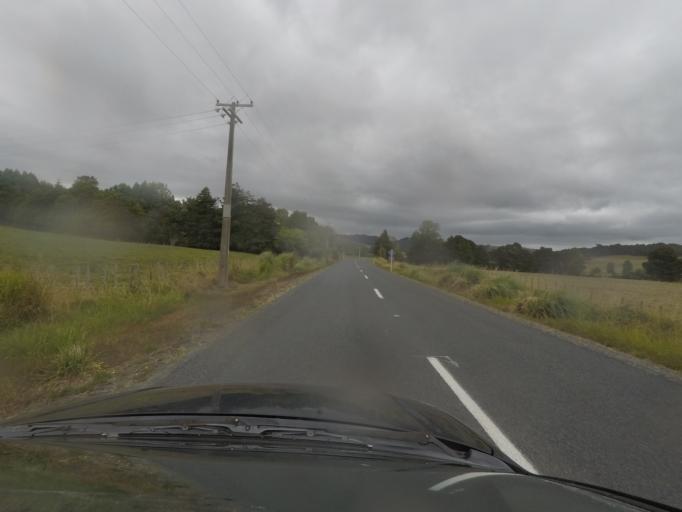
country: NZ
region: Auckland
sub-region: Auckland
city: Warkworth
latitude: -36.2793
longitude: 174.6710
